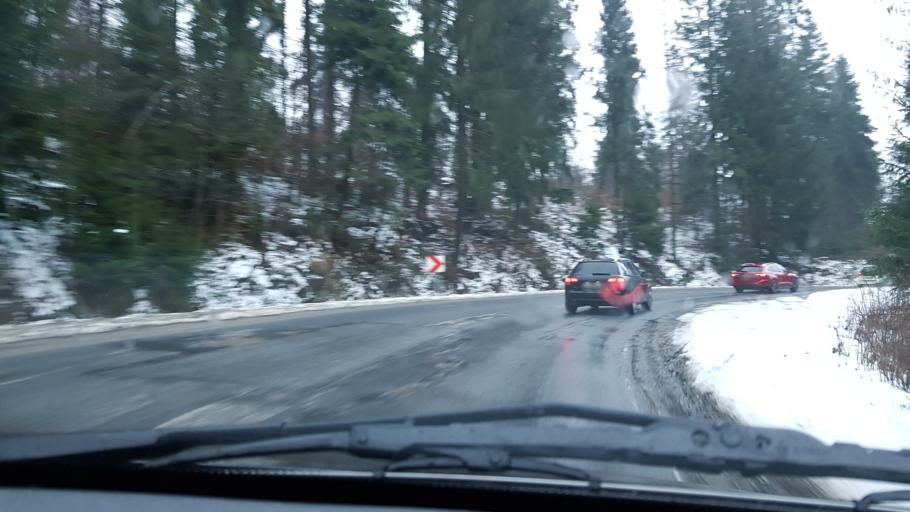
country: PL
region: Lesser Poland Voivodeship
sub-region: Powiat nowotarski
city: Sieniawa
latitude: 49.5138
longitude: 19.8976
